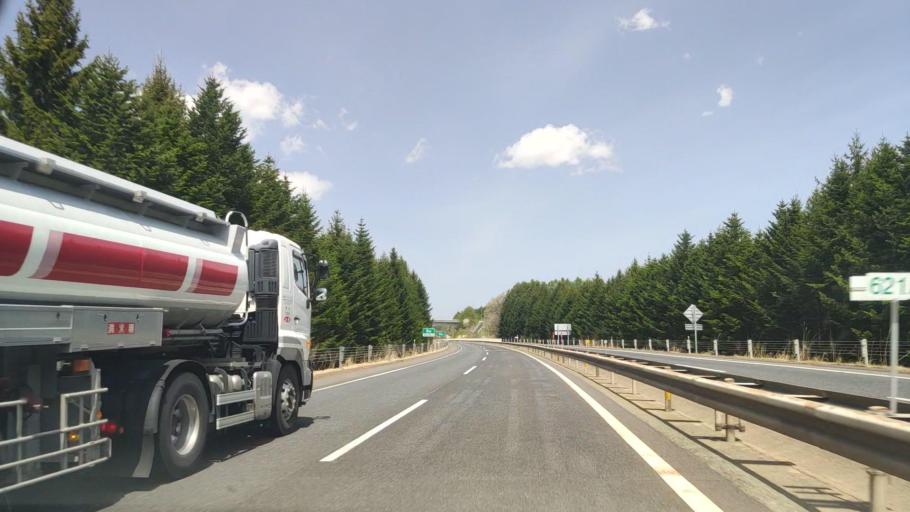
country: JP
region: Aomori
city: Hachinohe
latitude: 40.4127
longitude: 141.4435
